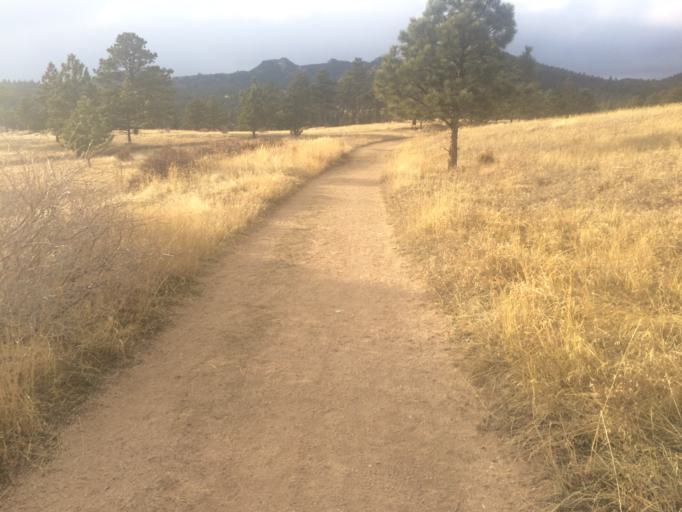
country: US
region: Colorado
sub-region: Boulder County
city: Coal Creek
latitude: 39.9581
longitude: -105.3410
